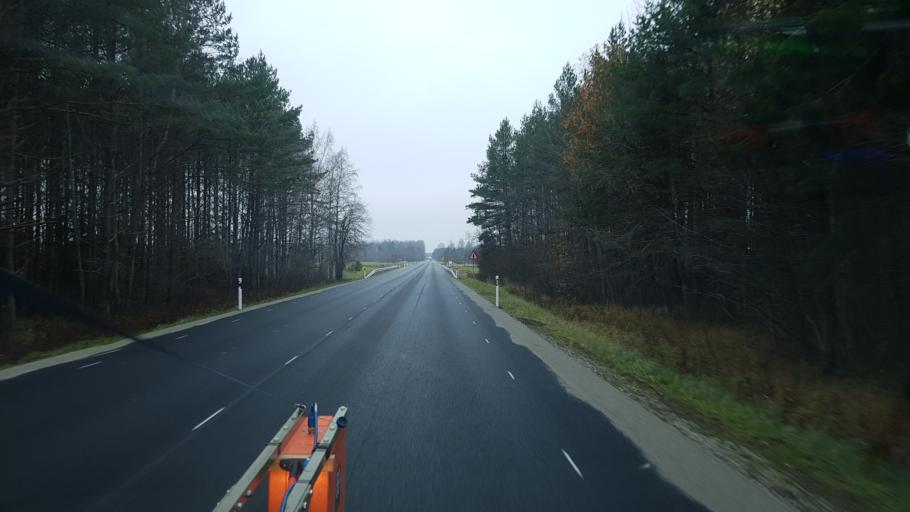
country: EE
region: Raplamaa
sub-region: Kehtna vald
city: Kehtna
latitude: 58.8483
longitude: 25.0349
